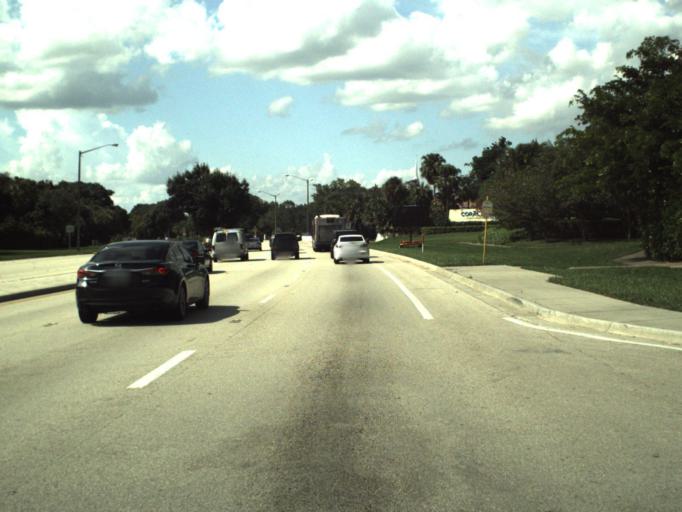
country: US
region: Florida
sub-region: Broward County
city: Tamarac
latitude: 26.2313
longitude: -80.2528
